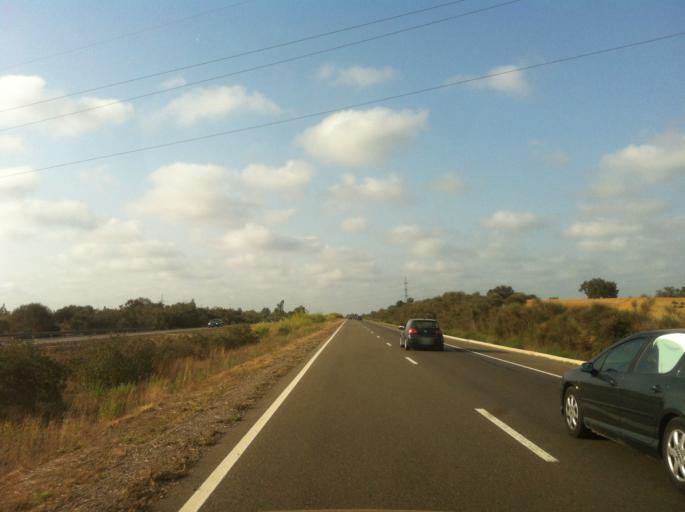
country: MA
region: Gharb-Chrarda-Beni Hssen
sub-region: Kenitra Province
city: Kenitra
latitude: 34.2275
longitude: -6.5557
